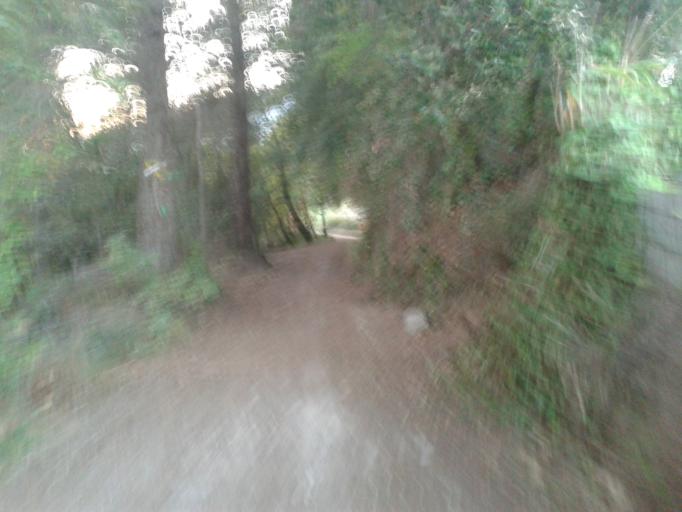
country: ES
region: Catalonia
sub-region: Provincia de Barcelona
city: Sentmenat
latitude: 41.6187
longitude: 2.1322
